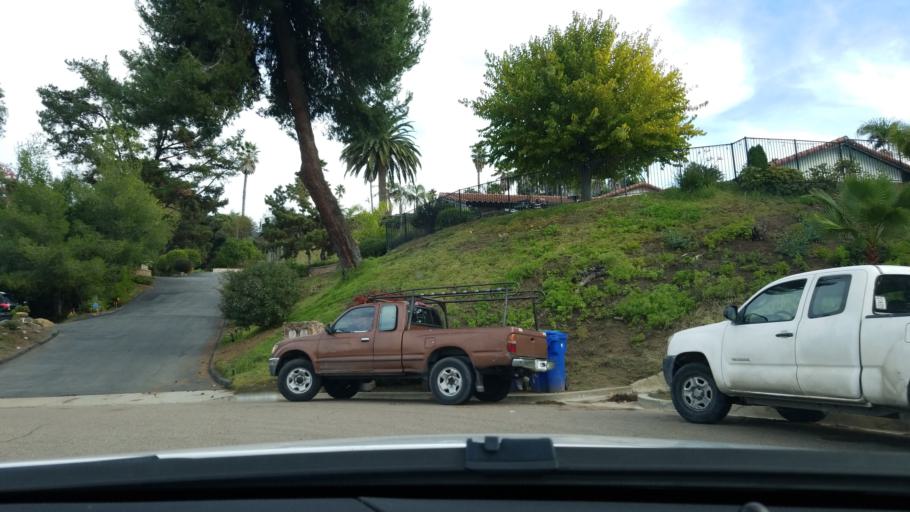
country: US
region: California
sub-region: San Diego County
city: Casa de Oro-Mount Helix
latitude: 32.7716
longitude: -116.9571
